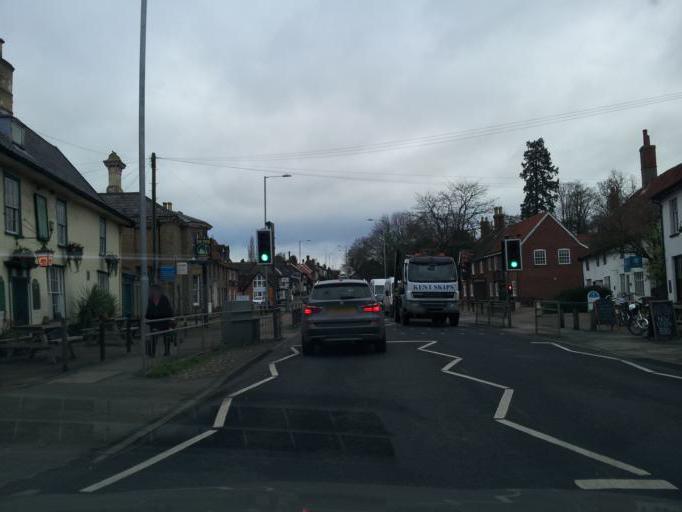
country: GB
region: England
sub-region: Norfolk
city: Long Stratton
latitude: 52.4882
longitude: 1.2348
